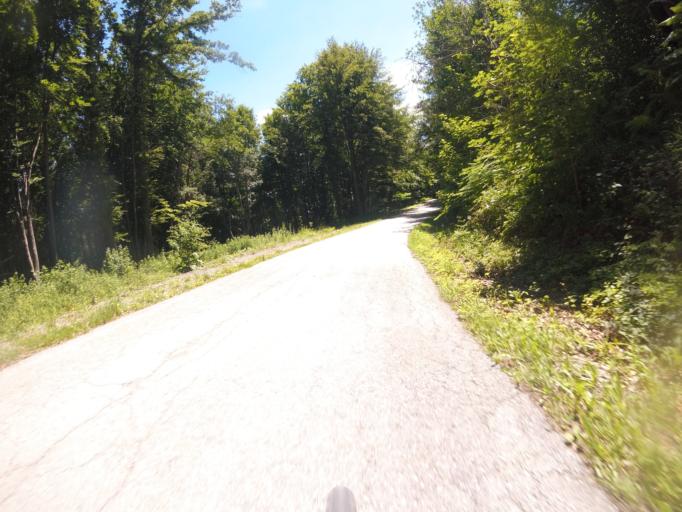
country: SI
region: Metlika
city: Metlika
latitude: 45.7151
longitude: 15.3847
